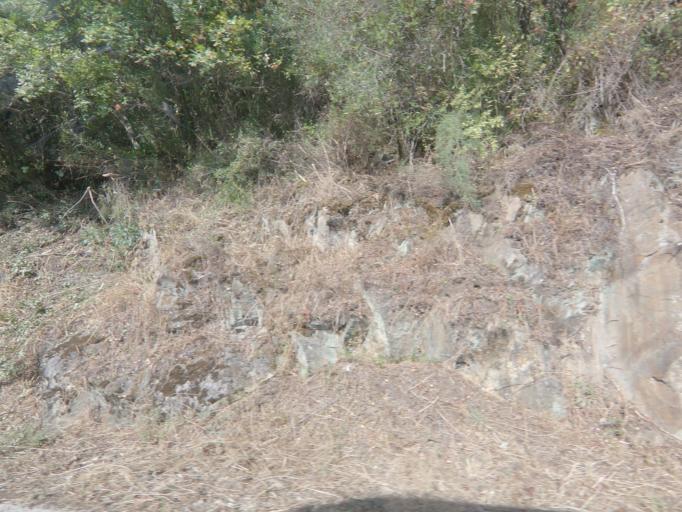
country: PT
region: Vila Real
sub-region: Sabrosa
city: Vilela
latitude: 41.2111
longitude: -7.5543
